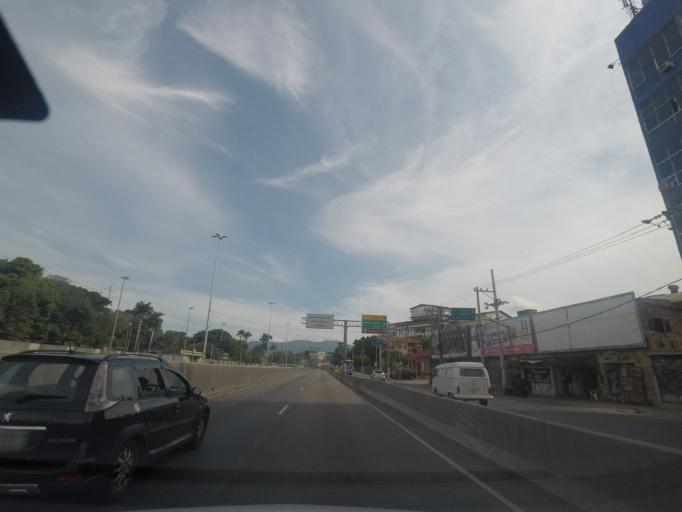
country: BR
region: Rio de Janeiro
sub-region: Rio De Janeiro
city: Rio de Janeiro
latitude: -22.8653
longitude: -43.2480
